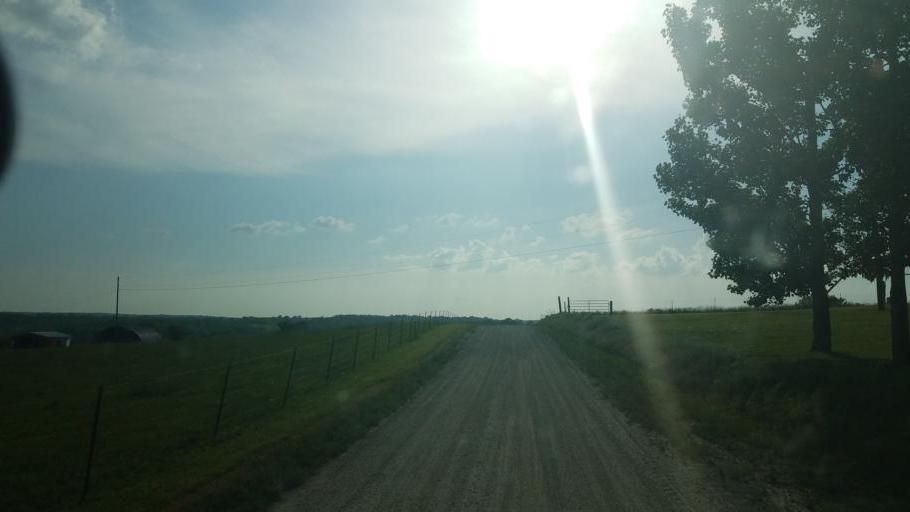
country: US
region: Missouri
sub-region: Moniteau County
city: California
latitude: 38.7522
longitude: -92.6150
